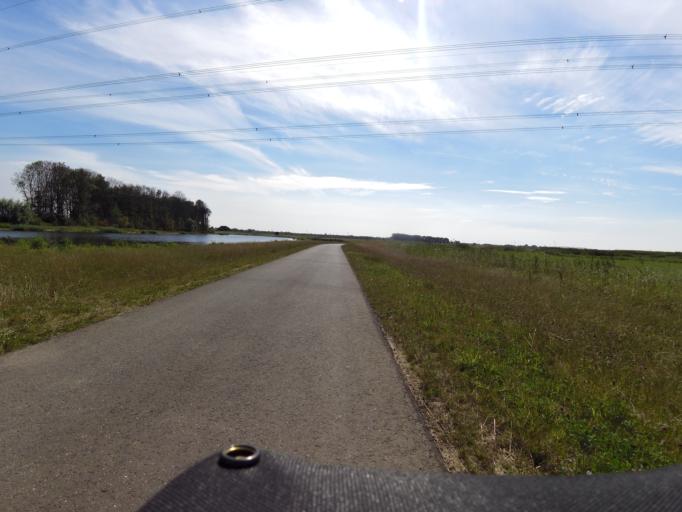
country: NL
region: South Holland
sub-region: Gemeente Hardinxveld-Giessendam
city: Neder-Hardinxveld
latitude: 51.7737
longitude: 4.8387
